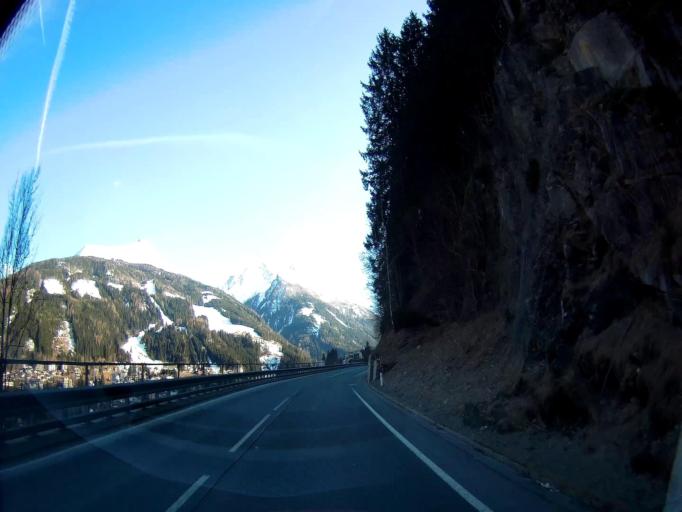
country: AT
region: Salzburg
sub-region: Politischer Bezirk Sankt Johann im Pongau
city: Bad Gastein
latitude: 47.1272
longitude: 13.1308
